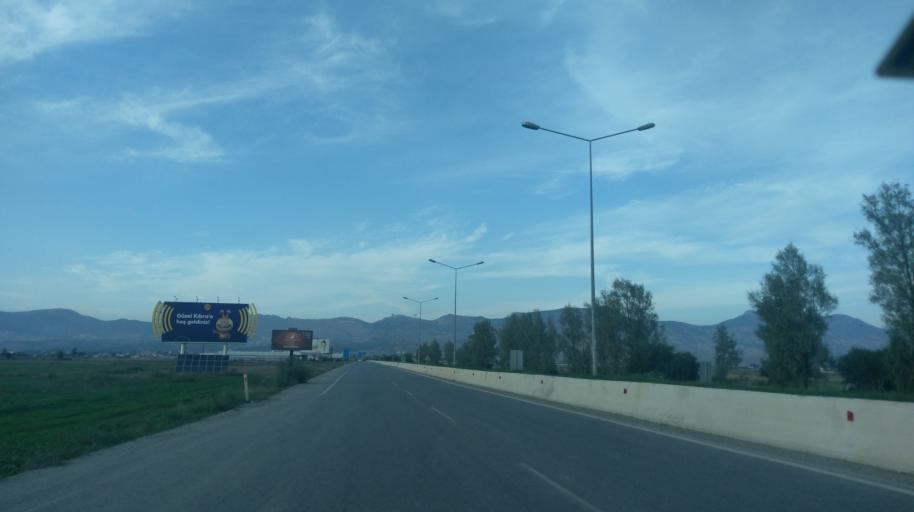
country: CY
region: Lefkosia
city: Geri
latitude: 35.2098
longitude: 33.4985
